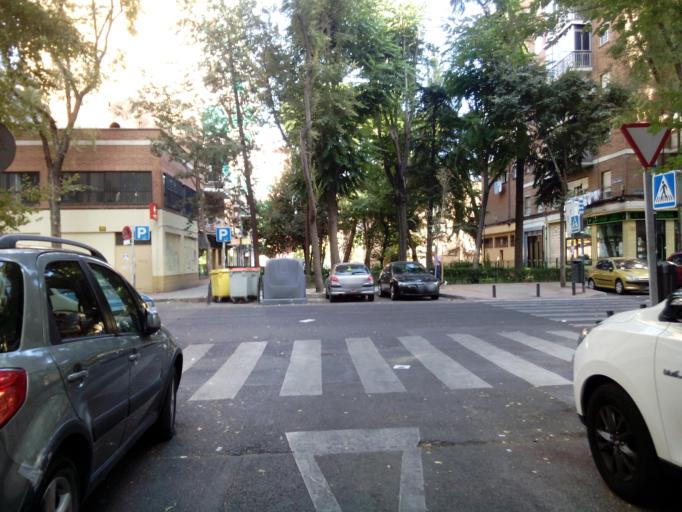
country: ES
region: Madrid
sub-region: Provincia de Madrid
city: Usera
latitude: 40.3921
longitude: -3.7100
